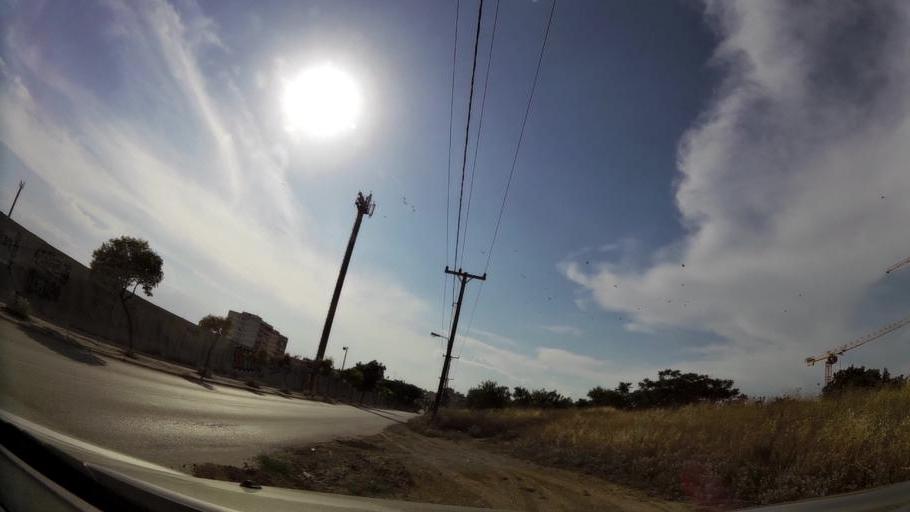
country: GR
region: Central Macedonia
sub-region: Nomos Thessalonikis
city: Kalamaria
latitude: 40.5664
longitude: 22.9663
